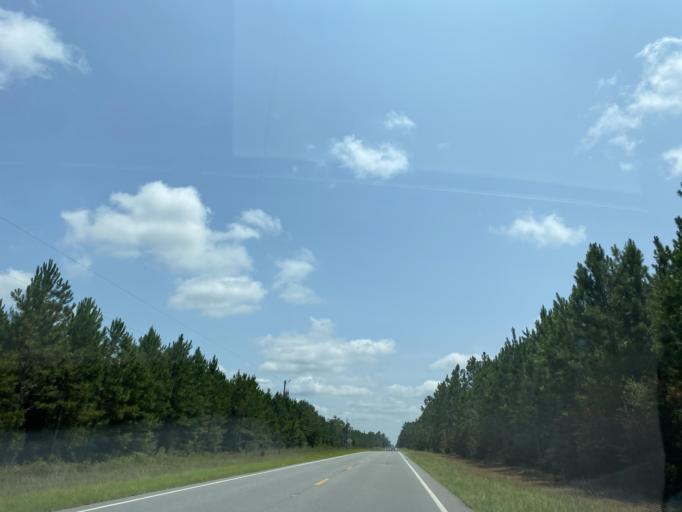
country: US
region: Georgia
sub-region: Jeff Davis County
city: Hazlehurst
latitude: 31.7485
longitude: -82.5447
